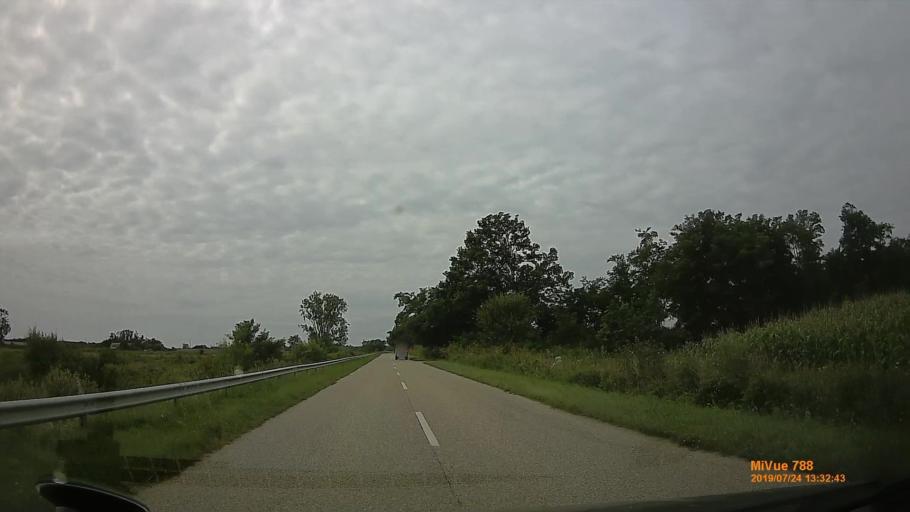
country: HU
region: Szabolcs-Szatmar-Bereg
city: Aranyosapati
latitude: 48.2284
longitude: 22.3336
